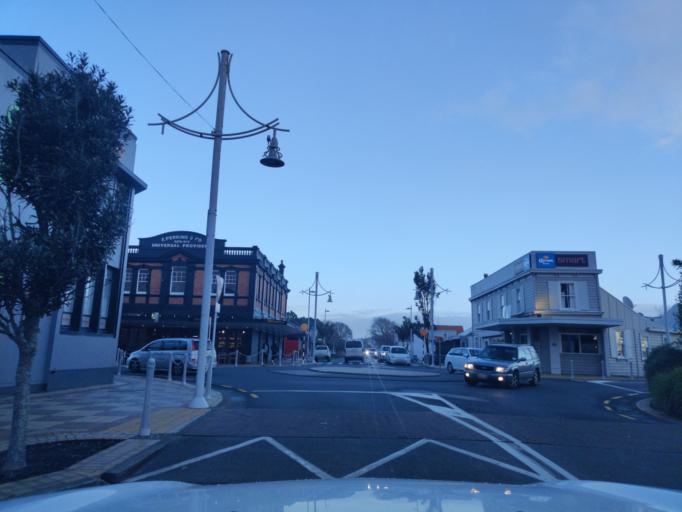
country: NZ
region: Auckland
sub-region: Auckland
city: Pukekohe East
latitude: -37.2002
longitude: 174.9012
